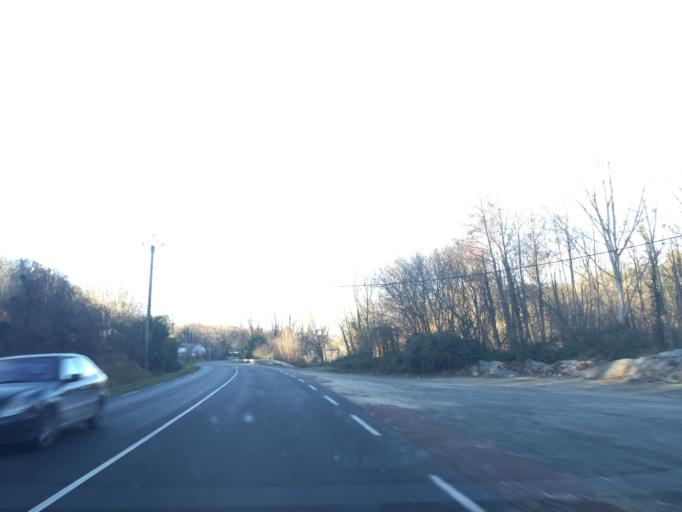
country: FR
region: Aquitaine
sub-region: Departement de la Dordogne
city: Neuvic
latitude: 45.1681
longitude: 0.3950
